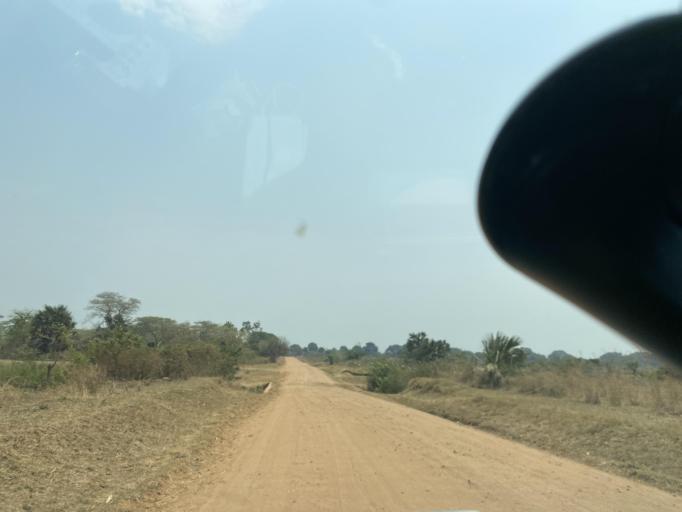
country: ZM
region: Lusaka
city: Kafue
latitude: -15.6297
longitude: 28.0990
